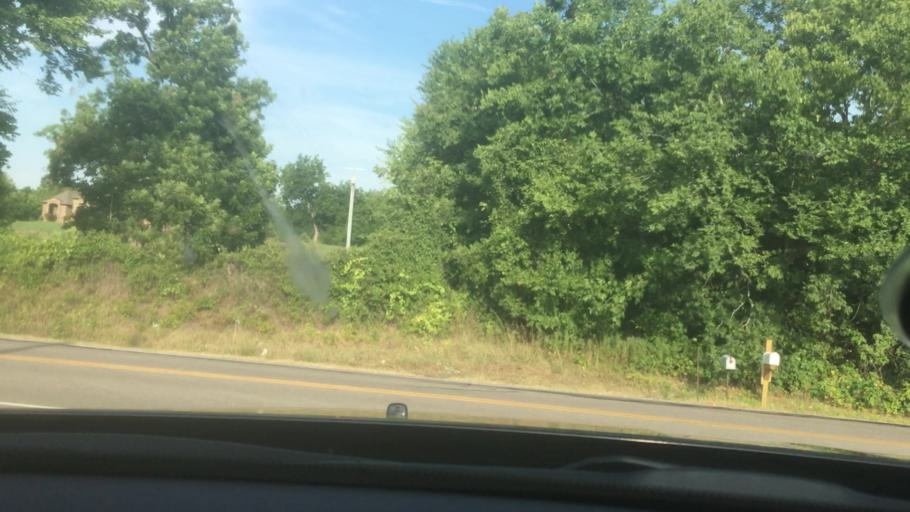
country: US
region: Oklahoma
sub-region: Pontotoc County
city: Ada
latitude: 34.7219
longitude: -96.6699
